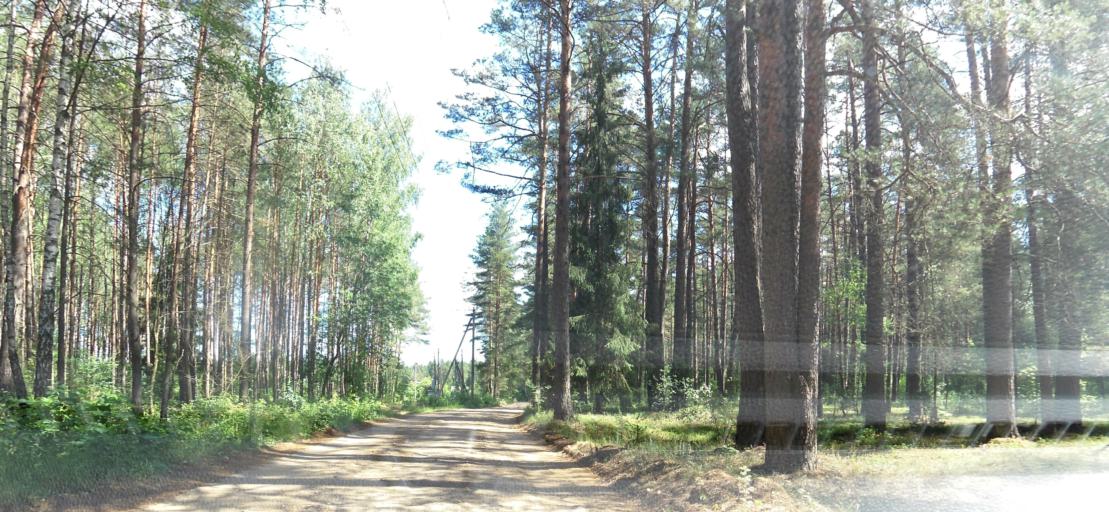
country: LT
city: Nemencine
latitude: 54.8231
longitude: 25.4088
